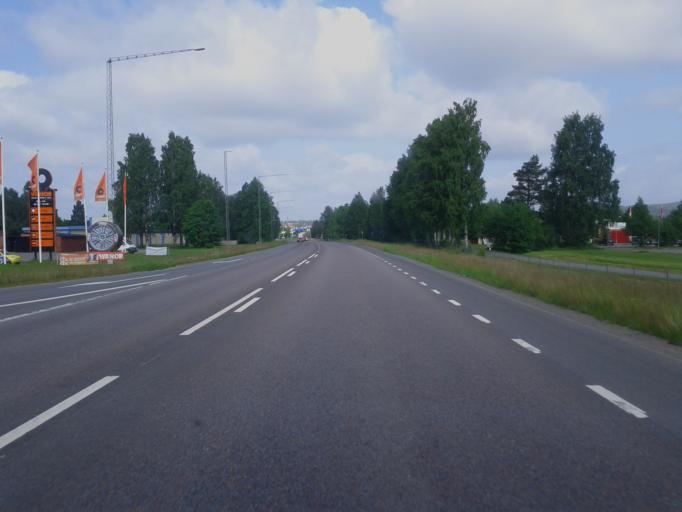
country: SE
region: Vaesterbotten
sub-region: Skelleftea Kommun
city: Skelleftea
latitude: 64.7392
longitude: 20.9644
